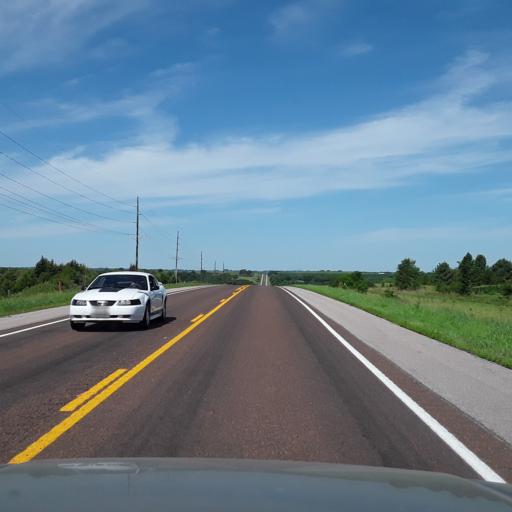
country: US
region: Nebraska
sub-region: Seward County
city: Milford
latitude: 40.8865
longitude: -96.8998
